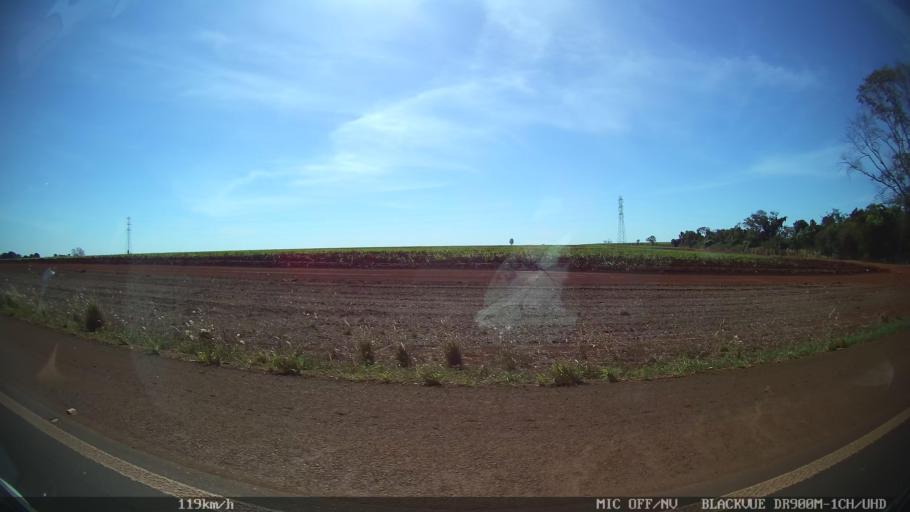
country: BR
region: Sao Paulo
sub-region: Guaira
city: Guaira
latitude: -20.4453
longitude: -48.4021
